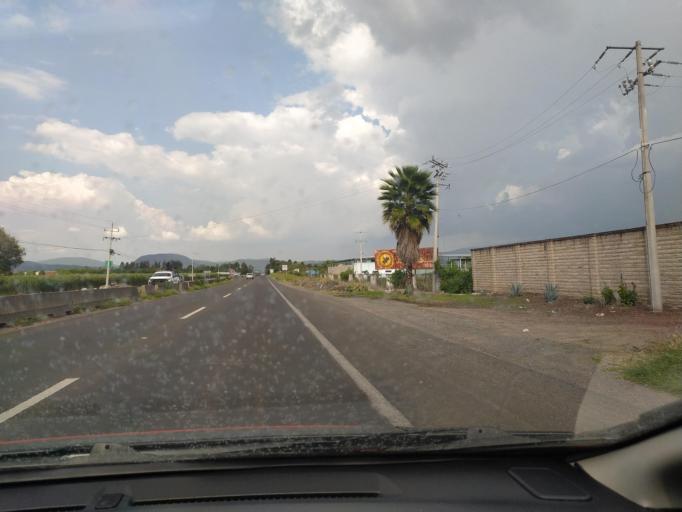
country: MX
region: Jalisco
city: Villa Corona
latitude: 20.4092
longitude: -103.6470
